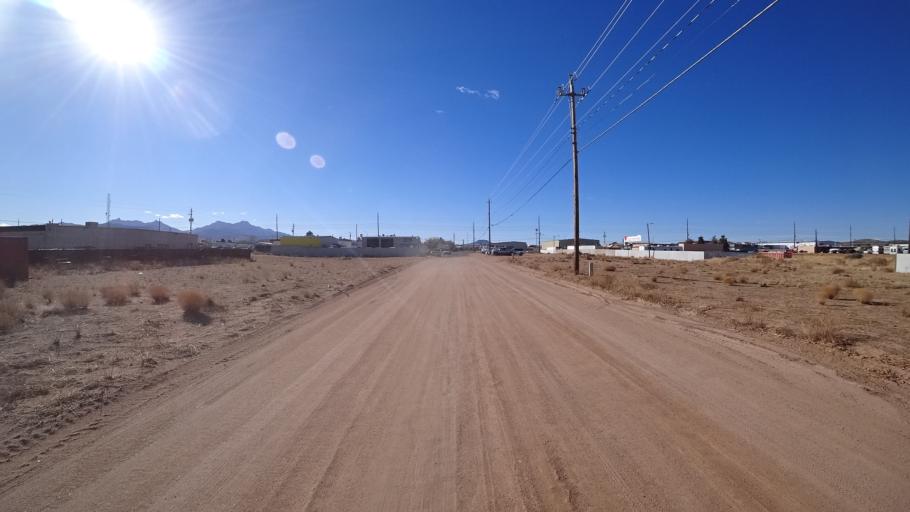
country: US
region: Arizona
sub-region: Mohave County
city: New Kingman-Butler
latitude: 35.2265
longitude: -114.0149
